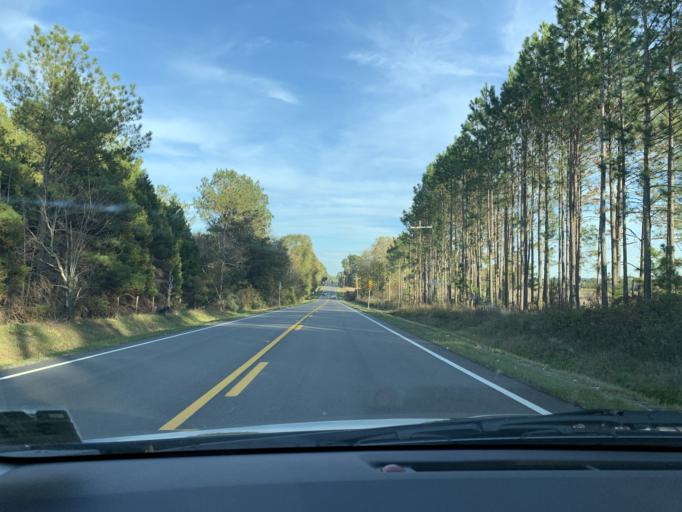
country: US
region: Georgia
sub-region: Irwin County
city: Ocilla
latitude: 31.5956
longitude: -83.1359
